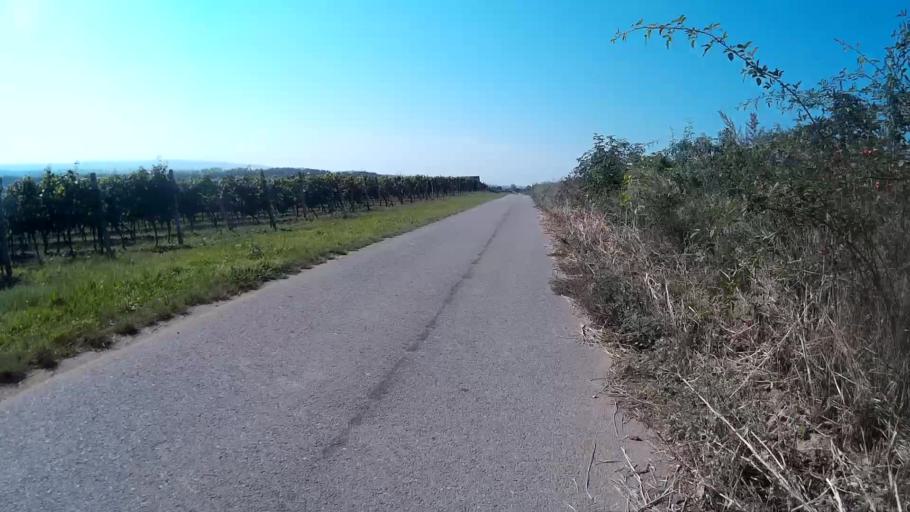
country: CZ
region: South Moravian
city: Novosedly
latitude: 48.8435
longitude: 16.5227
